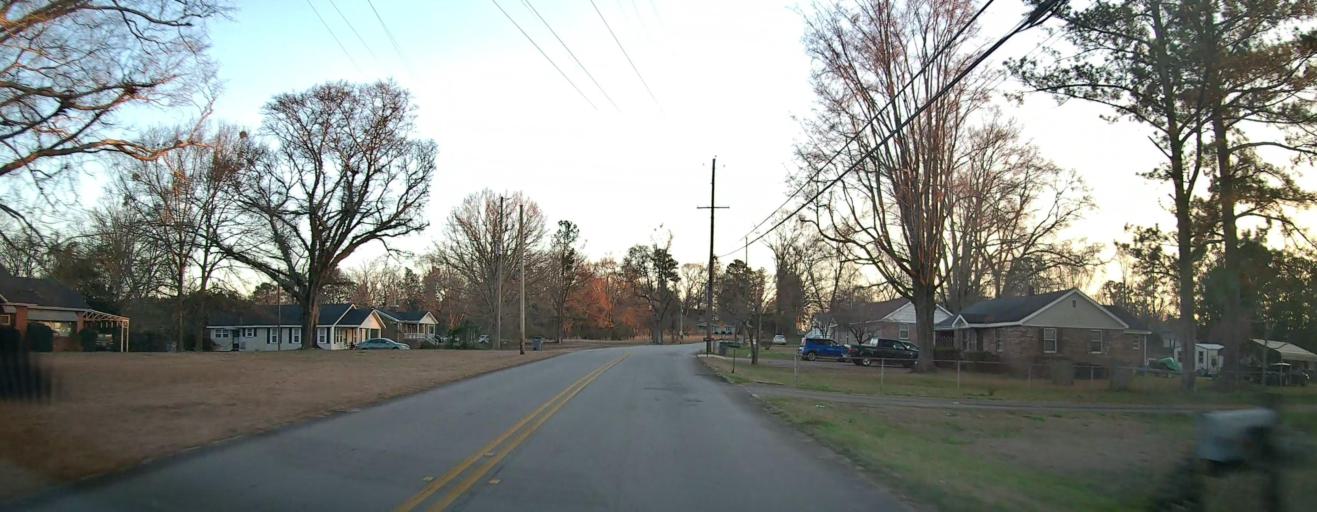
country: US
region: Georgia
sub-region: Troup County
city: La Grange
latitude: 33.0212
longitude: -85.0047
